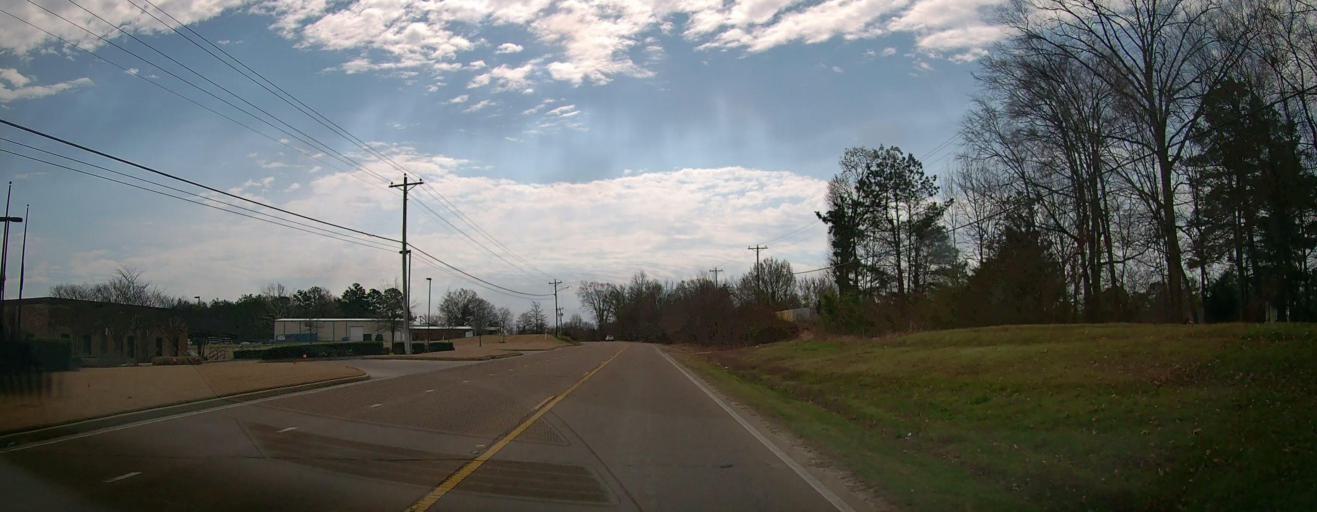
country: US
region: Mississippi
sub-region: De Soto County
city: Olive Branch
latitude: 34.9411
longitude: -89.8054
